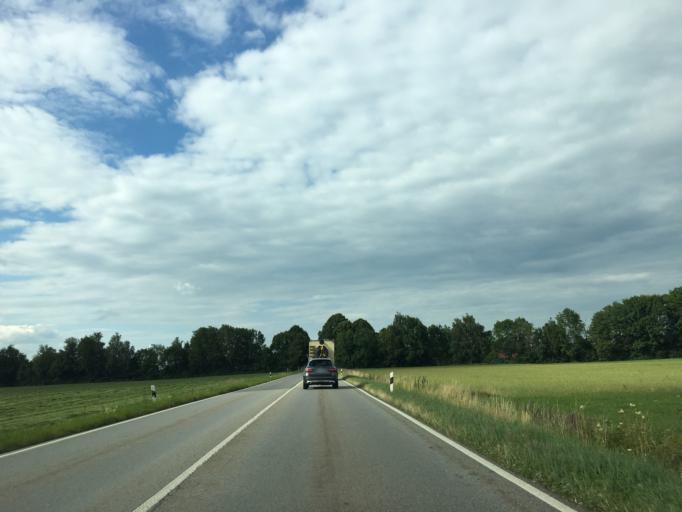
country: DE
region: Bavaria
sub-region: Upper Bavaria
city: Warngau
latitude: 47.8342
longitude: 11.7175
